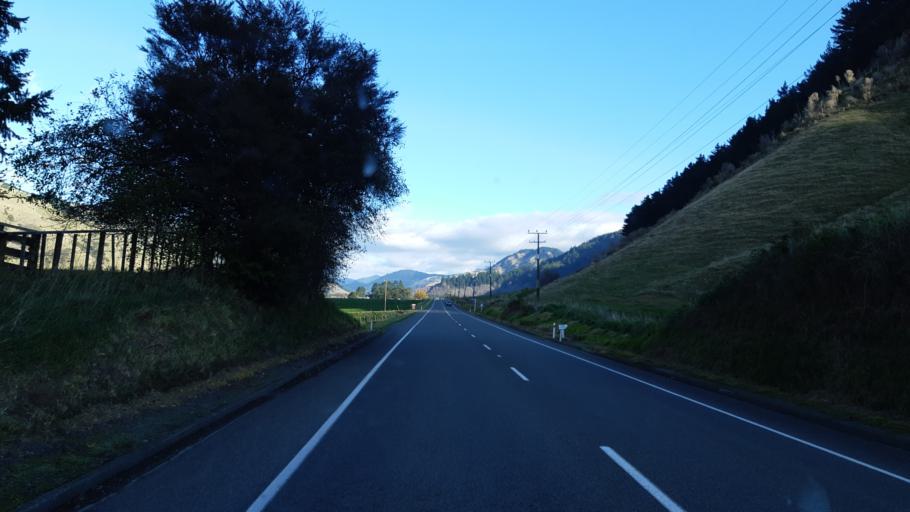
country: NZ
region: Marlborough
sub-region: Marlborough District
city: Picton
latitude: -41.3080
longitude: 173.7674
